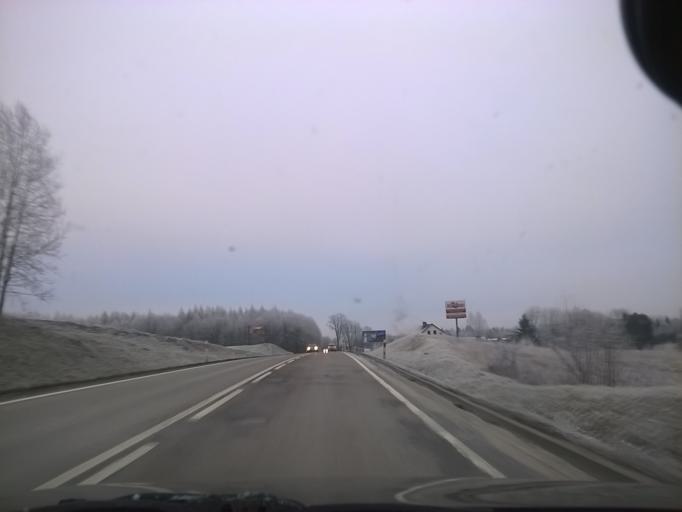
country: PL
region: Warmian-Masurian Voivodeship
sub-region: Powiat mragowski
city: Mragowo
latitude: 53.8521
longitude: 21.2387
